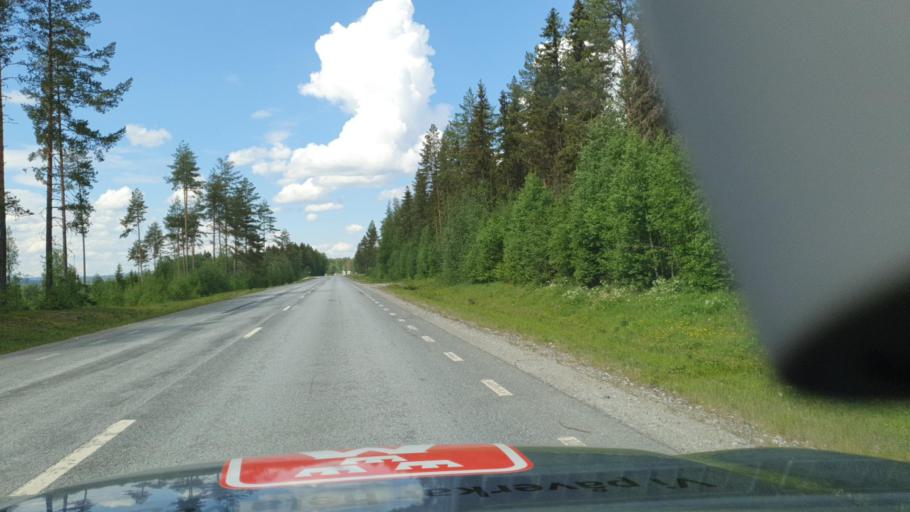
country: SE
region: Vaesternorrland
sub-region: Solleftea Kommun
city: As
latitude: 63.4398
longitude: 16.9253
